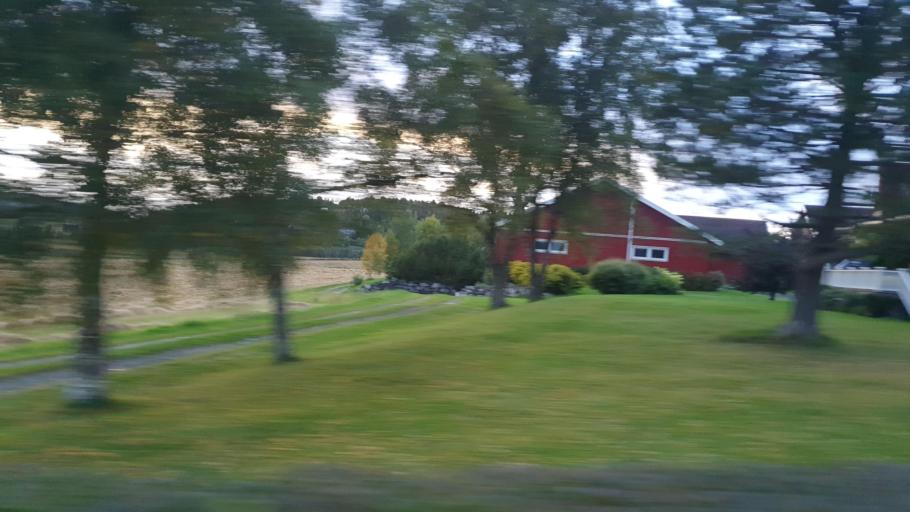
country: NO
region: Nord-Trondelag
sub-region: Levanger
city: Skogn
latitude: 63.6932
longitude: 11.1940
